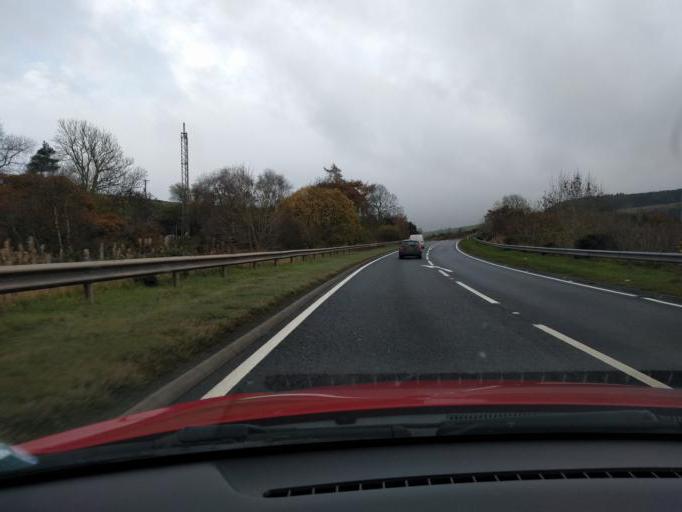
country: GB
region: Scotland
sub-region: The Scottish Borders
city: Chirnside
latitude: 55.8777
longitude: -2.2837
